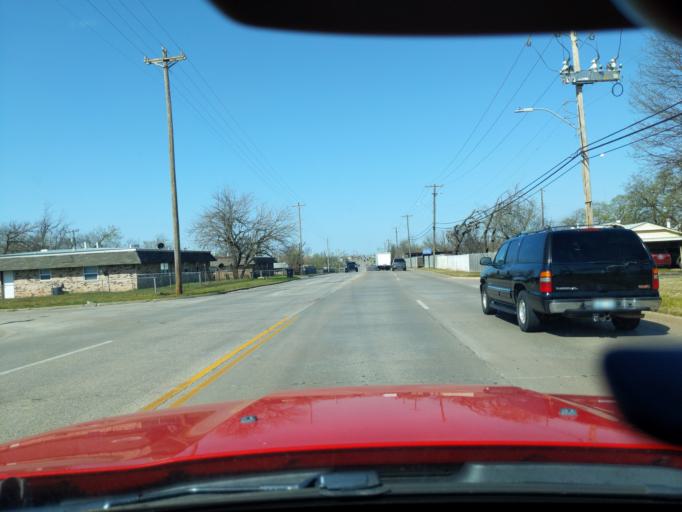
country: US
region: Oklahoma
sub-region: Cleveland County
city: Moore
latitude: 35.3488
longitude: -97.4858
